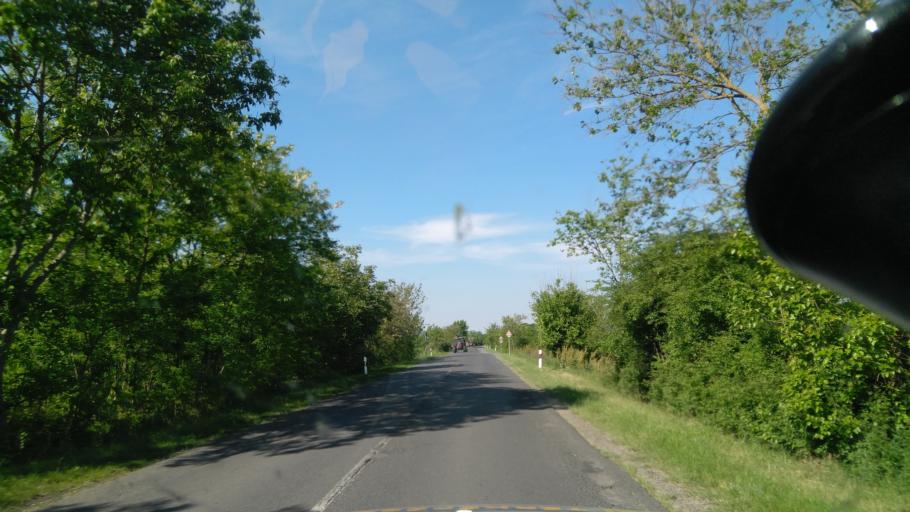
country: HU
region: Bekes
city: Gyula
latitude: 46.6808
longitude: 21.3046
